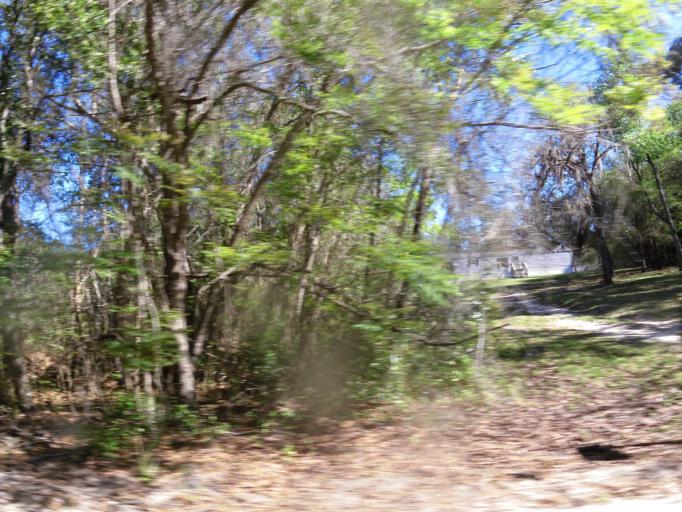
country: US
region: Florida
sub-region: Clay County
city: Keystone Heights
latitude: 29.8071
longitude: -82.0442
